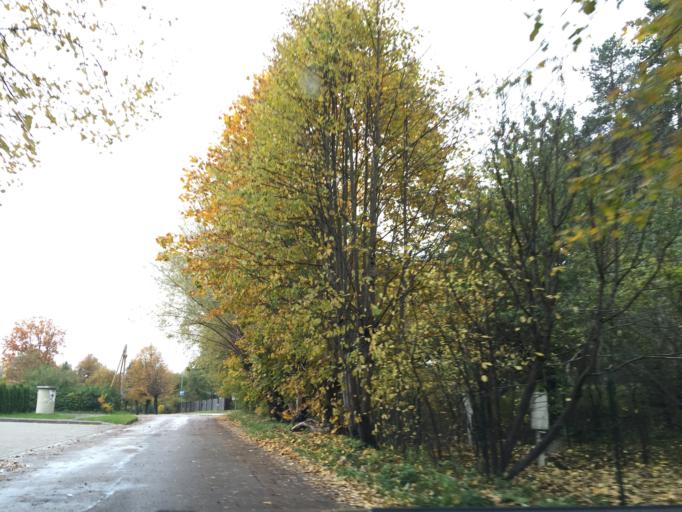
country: LV
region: Ogre
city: Ogre
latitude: 56.8084
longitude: 24.6216
